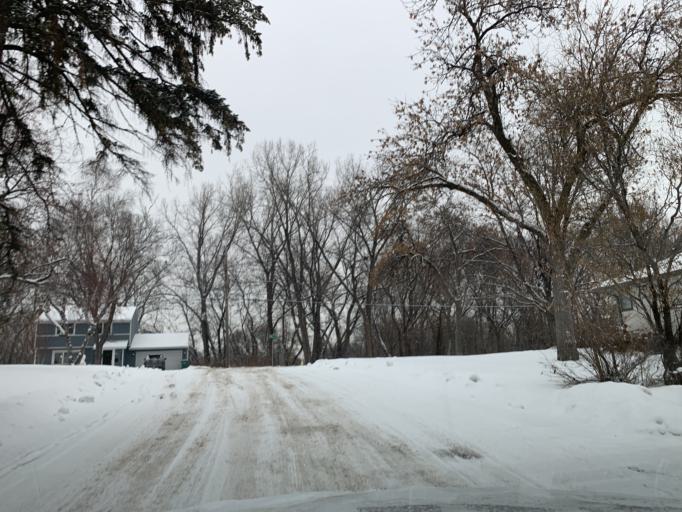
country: US
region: Minnesota
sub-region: Hennepin County
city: Saint Louis Park
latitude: 44.9518
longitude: -93.3378
